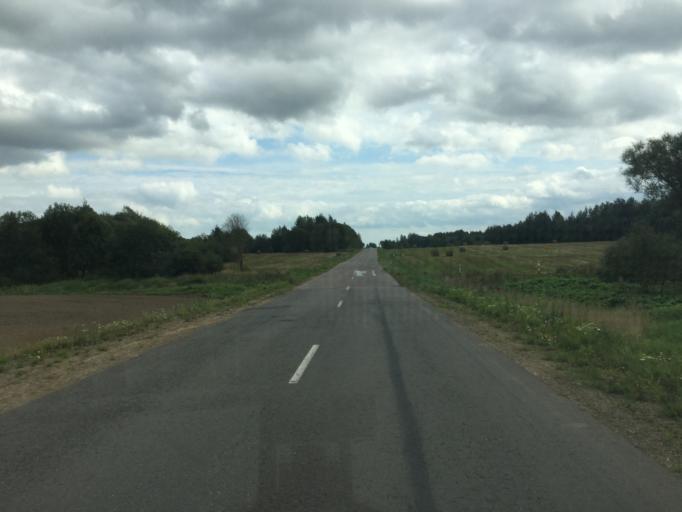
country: BY
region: Vitebsk
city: Vitebsk
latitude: 55.1322
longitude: 30.3098
